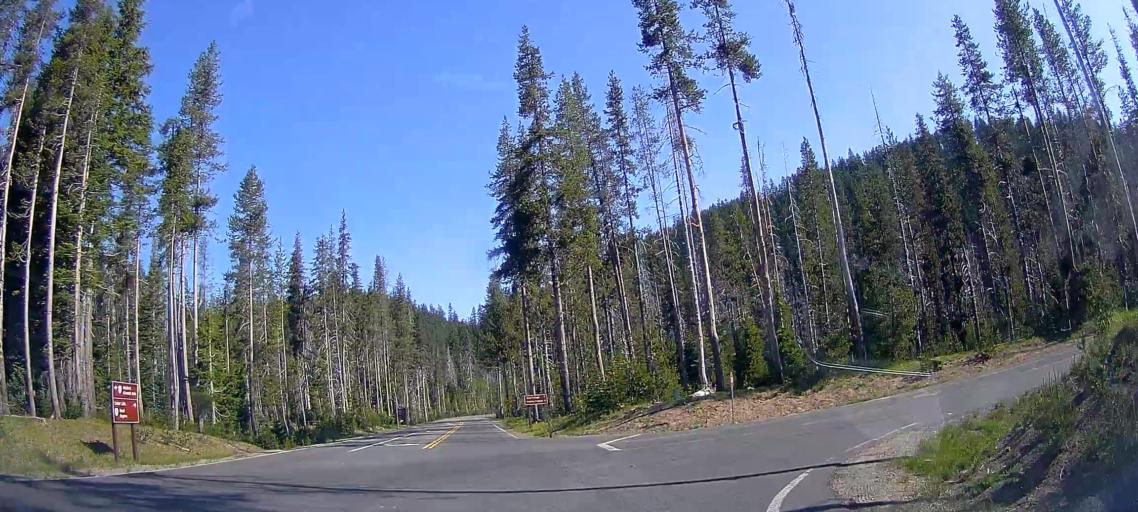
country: US
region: Oregon
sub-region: Jackson County
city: Shady Cove
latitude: 42.8694
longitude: -122.1694
